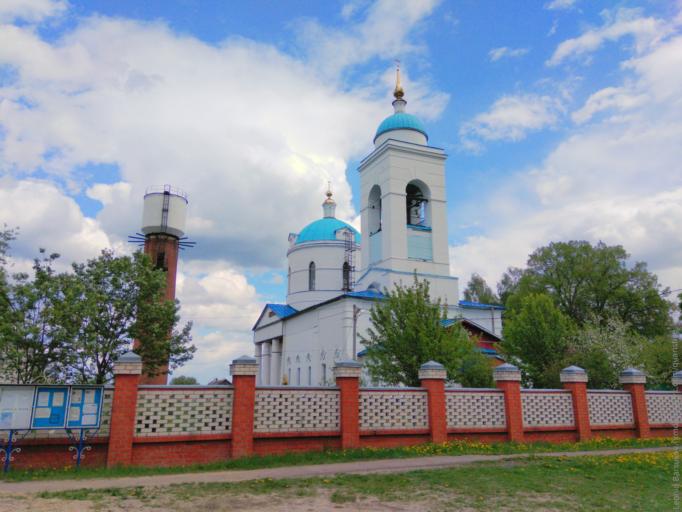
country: RU
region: Moskovskaya
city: Cherusti
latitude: 55.5970
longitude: 40.0227
